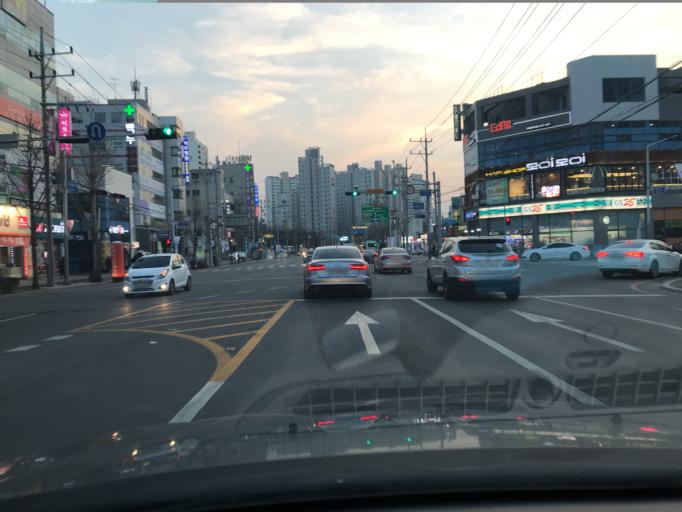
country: KR
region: Daegu
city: Hwawon
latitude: 35.8122
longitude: 128.5180
